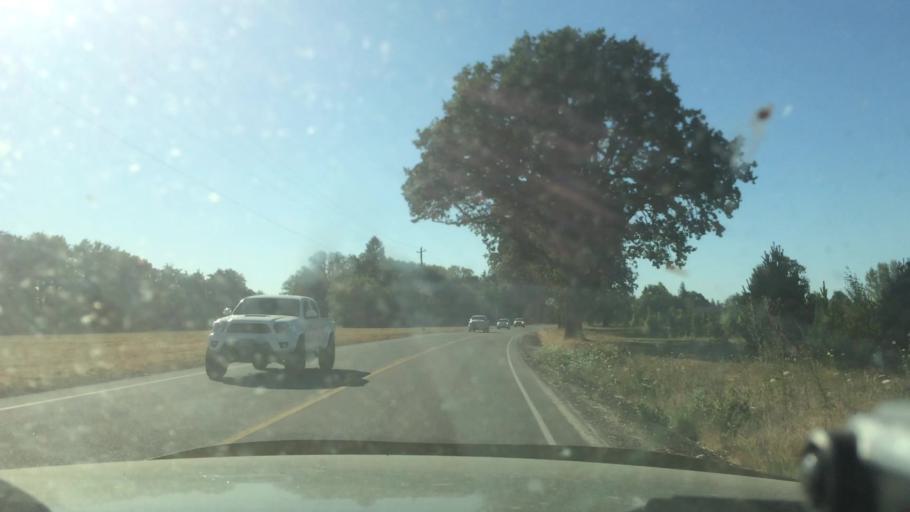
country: US
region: Oregon
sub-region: Marion County
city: Gervais
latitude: 45.1298
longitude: -122.9999
